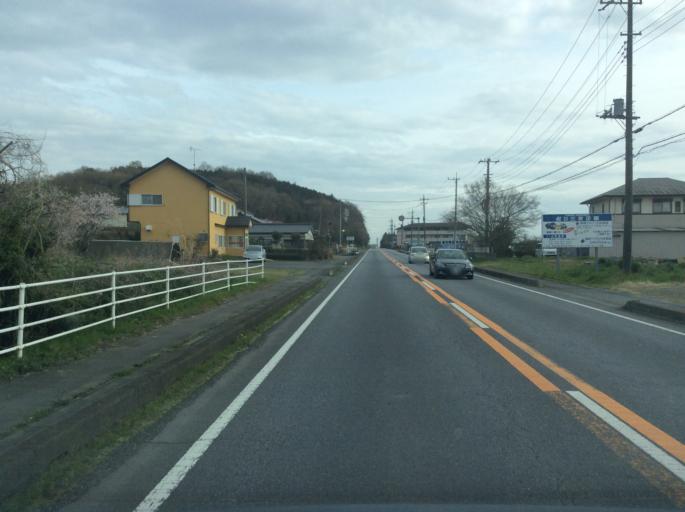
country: JP
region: Ibaraki
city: Tsukuba
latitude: 36.1658
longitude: 140.1068
